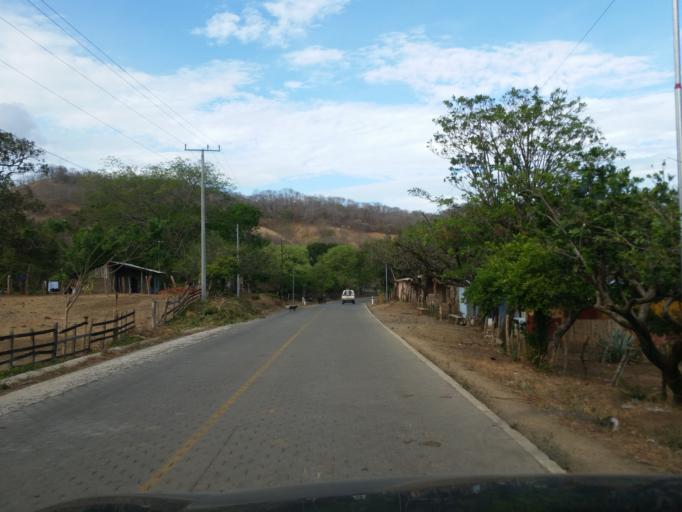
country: NI
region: Rivas
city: Tola
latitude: 11.3931
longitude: -85.9689
